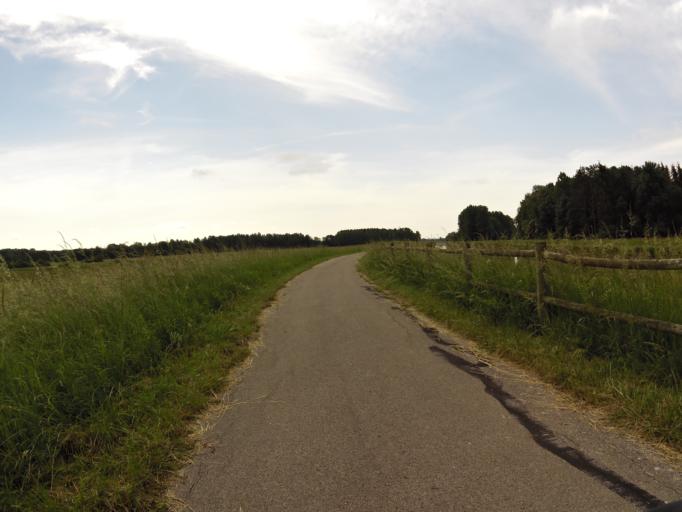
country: FR
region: Champagne-Ardenne
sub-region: Departement de l'Aube
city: Lusigny-sur-Barse
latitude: 48.2702
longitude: 4.2620
